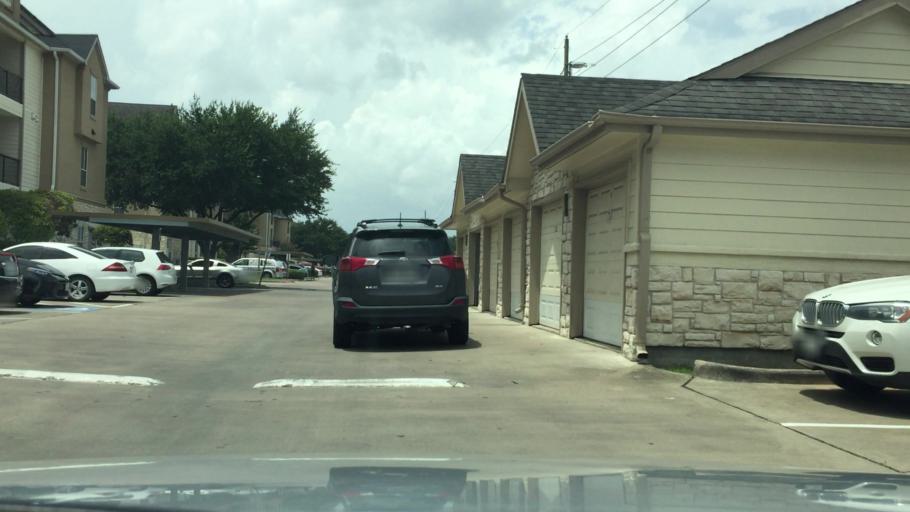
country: US
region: Texas
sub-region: Harris County
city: Bellaire
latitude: 29.7234
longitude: -95.4694
